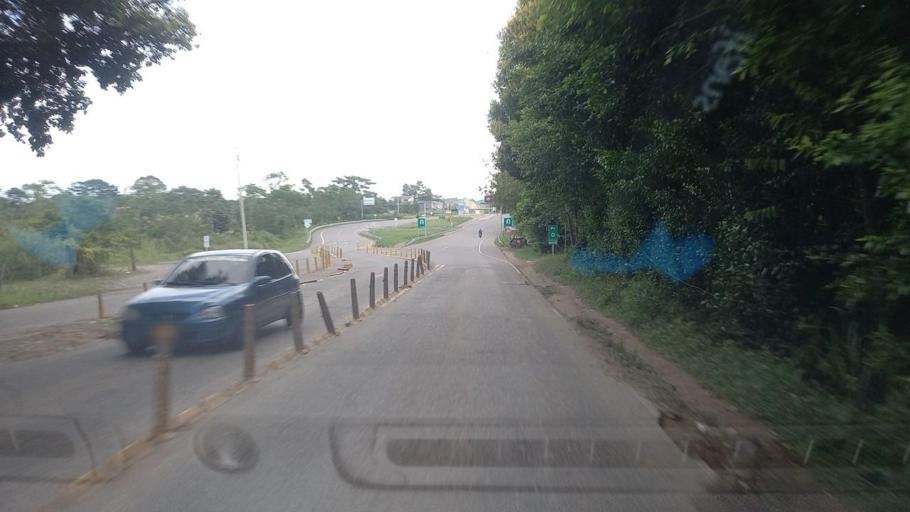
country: CO
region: Santander
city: Sabana de Torres
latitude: 7.1315
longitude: -73.5598
